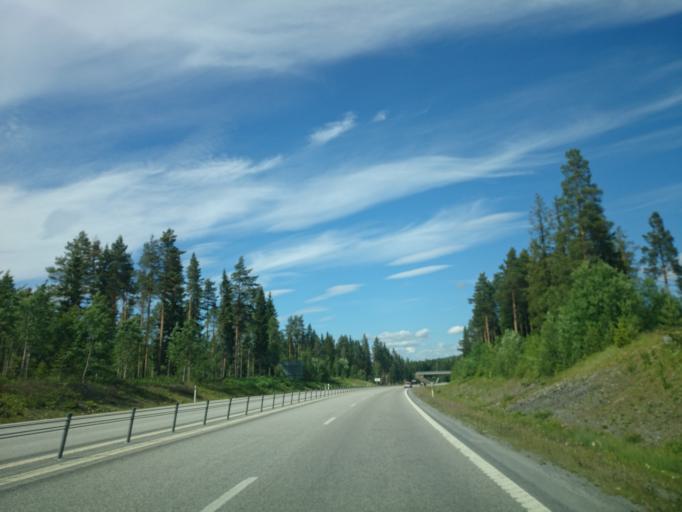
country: SE
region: Jaemtland
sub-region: OEstersunds Kommun
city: Ostersund
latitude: 63.1825
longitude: 14.6889
